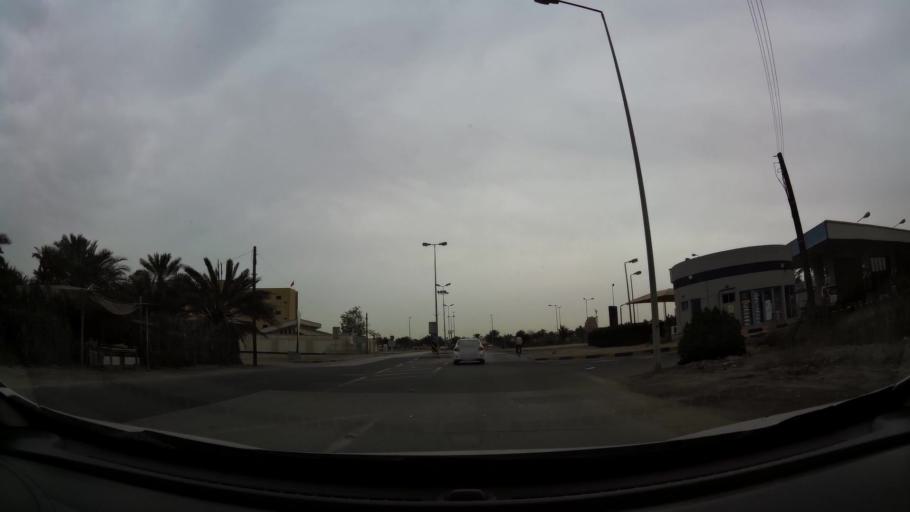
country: BH
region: Manama
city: Jidd Hafs
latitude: 26.1998
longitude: 50.5528
